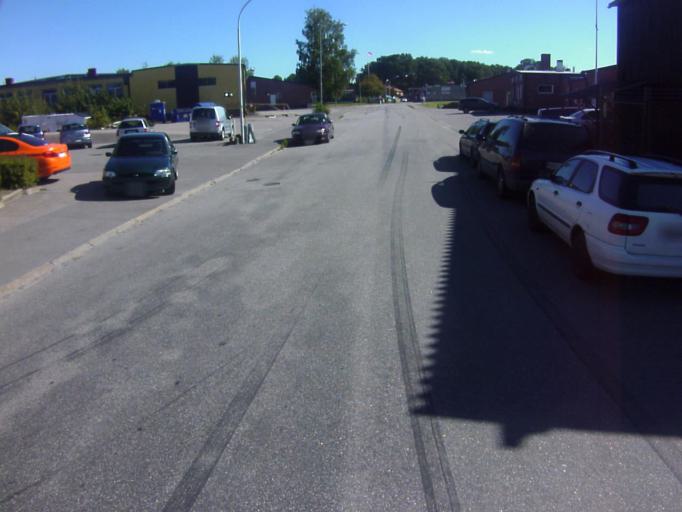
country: SE
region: Soedermanland
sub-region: Eskilstuna Kommun
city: Eskilstuna
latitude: 59.3835
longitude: 16.5074
